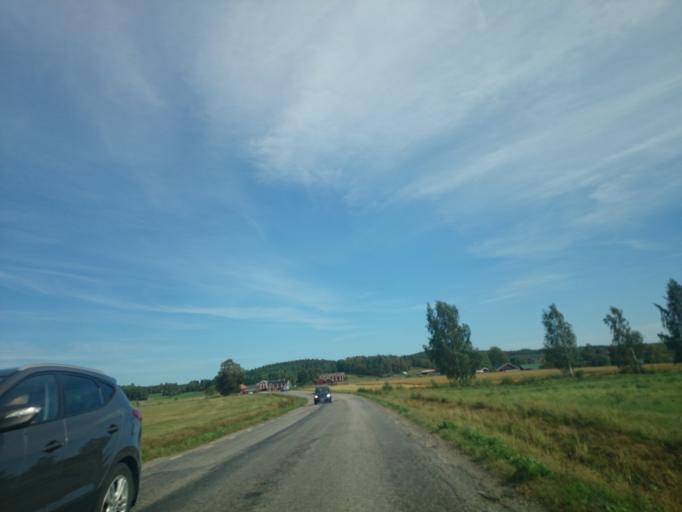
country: SE
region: Gaevleborg
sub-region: Hudiksvalls Kommun
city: Sorforsa
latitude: 61.7583
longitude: 16.8995
